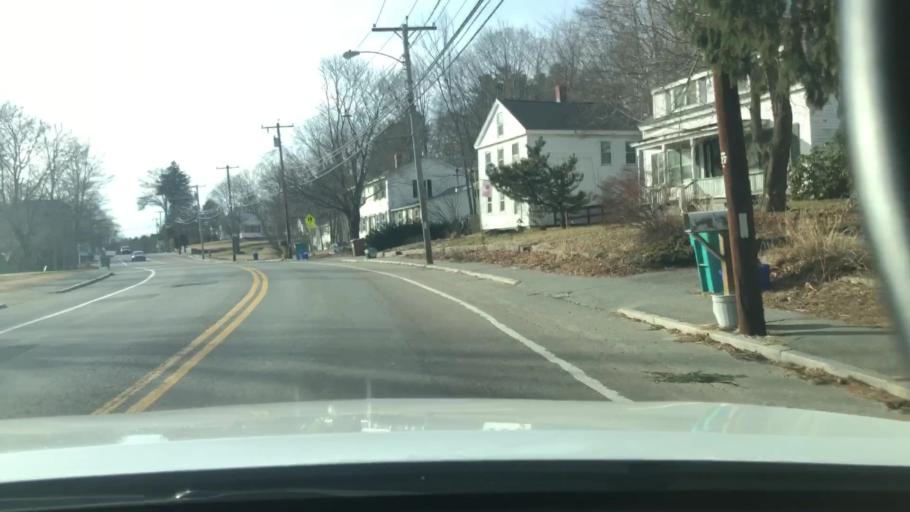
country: US
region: Massachusetts
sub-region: Worcester County
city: Upton
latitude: 42.1704
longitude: -71.6094
